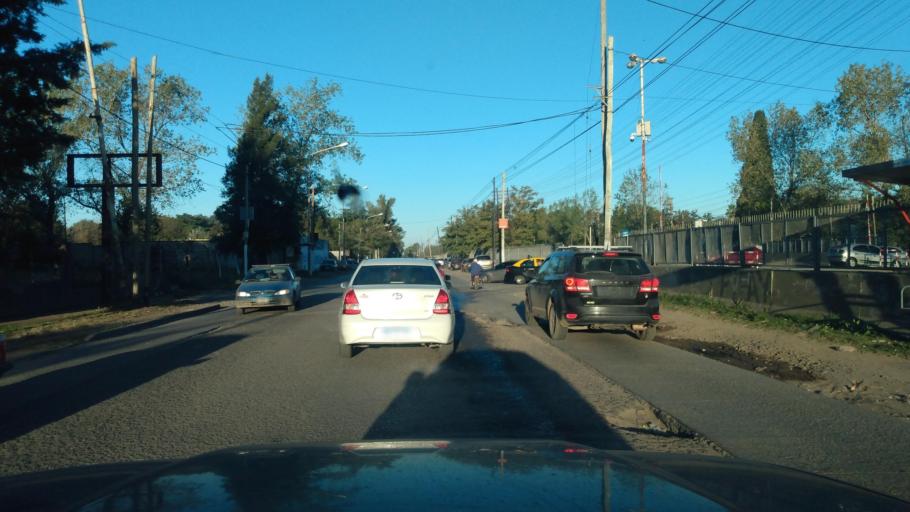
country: AR
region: Buenos Aires
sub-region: Partido de Merlo
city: Merlo
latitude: -34.6428
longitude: -58.8167
